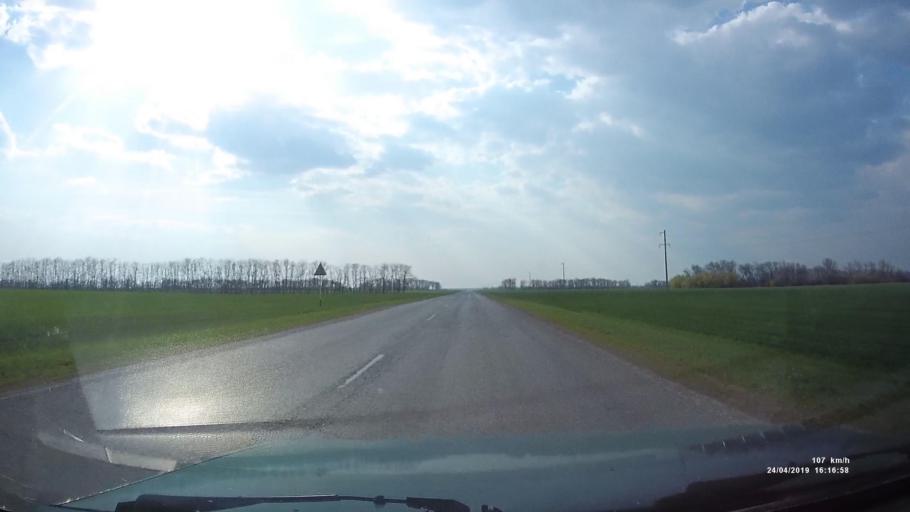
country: RU
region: Rostov
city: Sovetskoye
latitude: 46.7663
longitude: 42.1484
